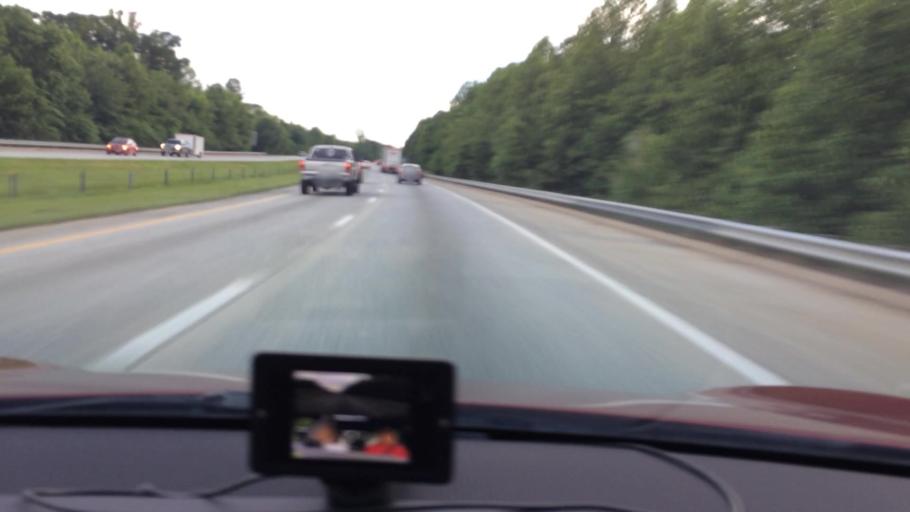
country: US
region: North Carolina
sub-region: Forsyth County
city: Kernersville
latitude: 36.0818
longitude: -80.0918
